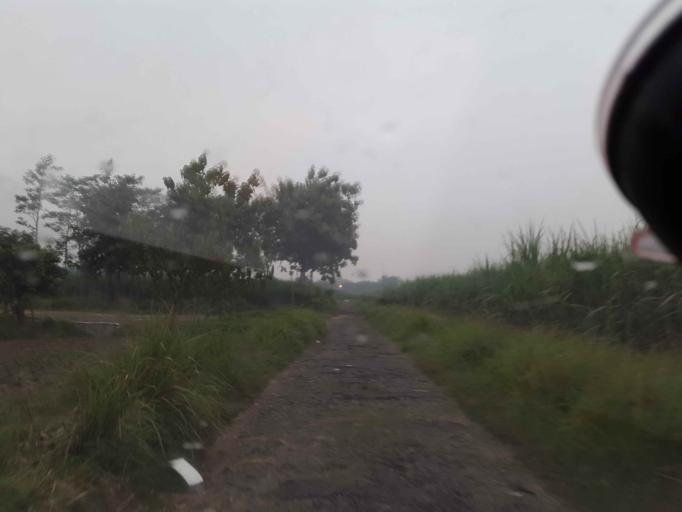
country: ID
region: Central Java
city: Adiwerna
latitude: -6.9540
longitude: 109.1341
